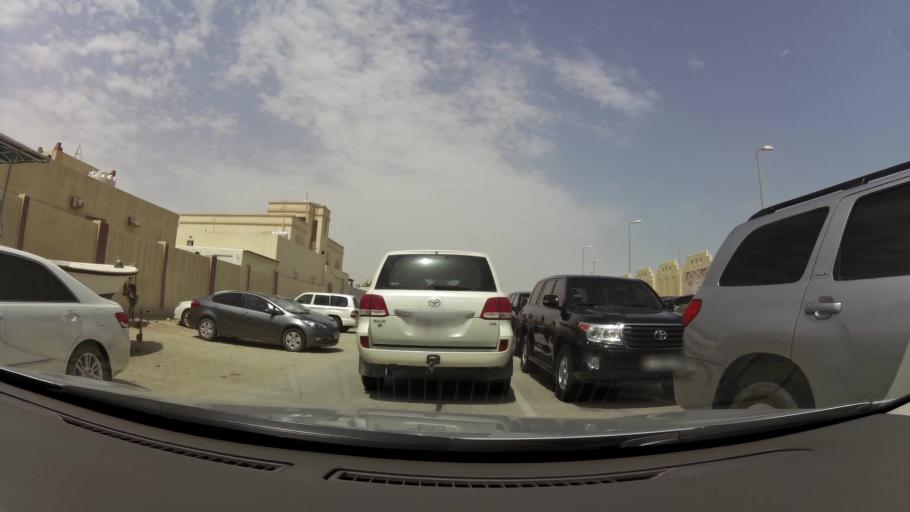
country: QA
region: Baladiyat ar Rayyan
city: Ar Rayyan
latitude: 25.3537
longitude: 51.4764
